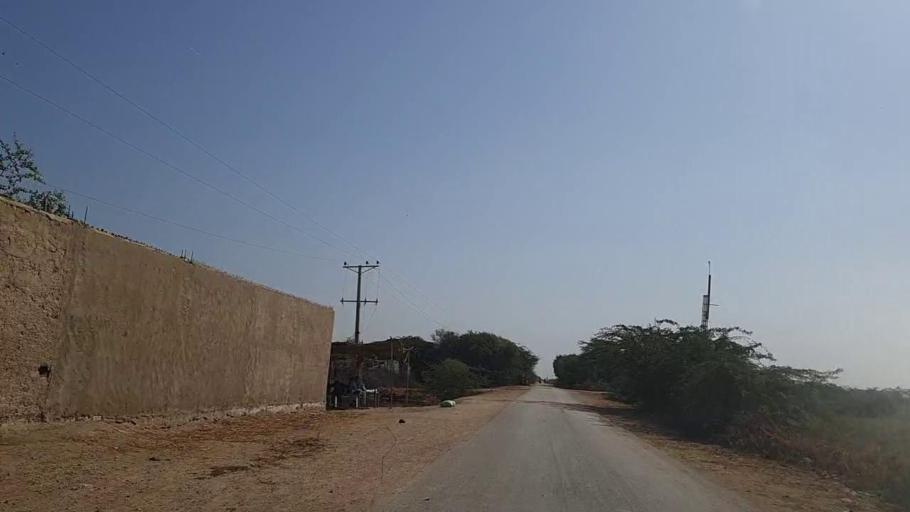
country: PK
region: Sindh
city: Mirpur Batoro
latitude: 24.6397
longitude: 68.2910
